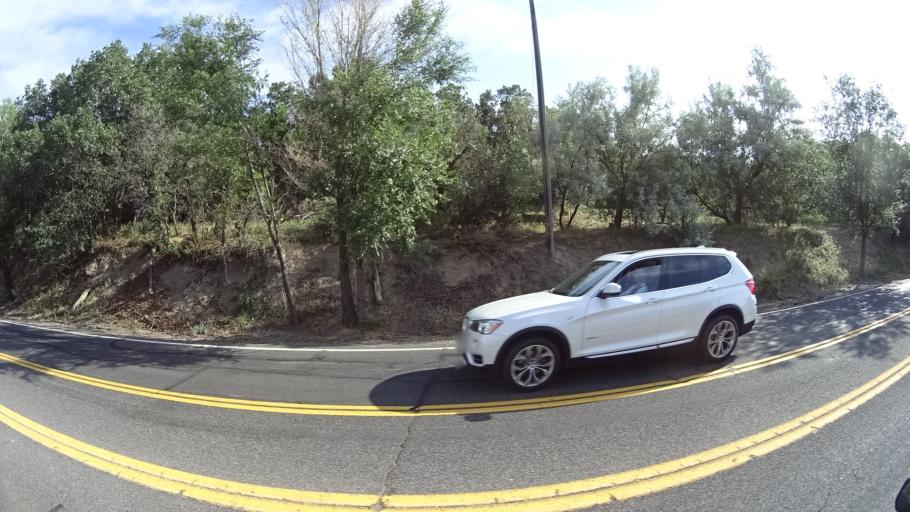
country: US
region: Colorado
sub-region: El Paso County
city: Air Force Academy
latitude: 38.9421
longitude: -104.8428
